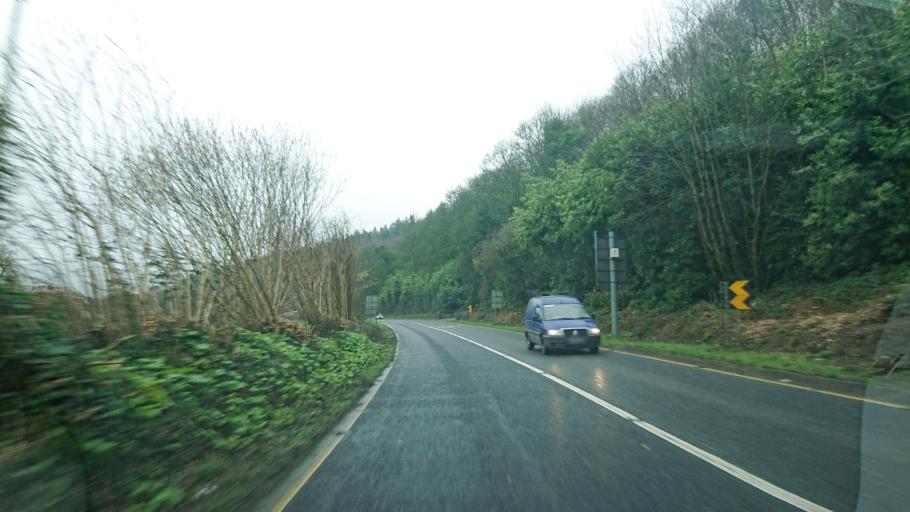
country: IE
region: Munster
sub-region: County Cork
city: Bandon
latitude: 51.7658
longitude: -8.6697
